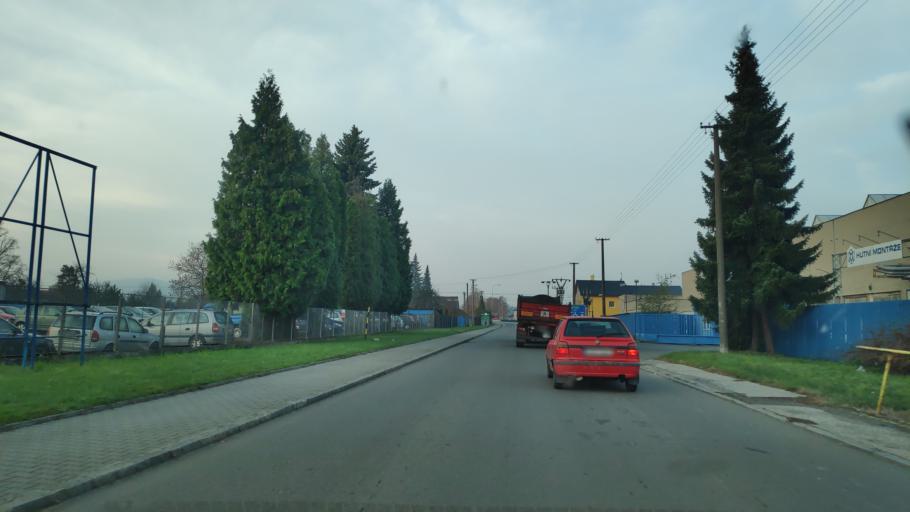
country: CZ
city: Sviadnov
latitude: 49.6961
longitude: 18.3234
